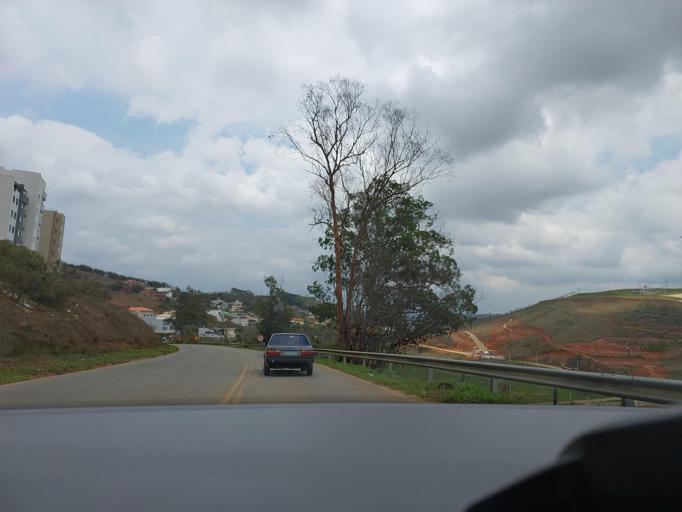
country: BR
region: Minas Gerais
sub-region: Ponte Nova
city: Ponte Nova
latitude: -20.3949
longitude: -42.8763
